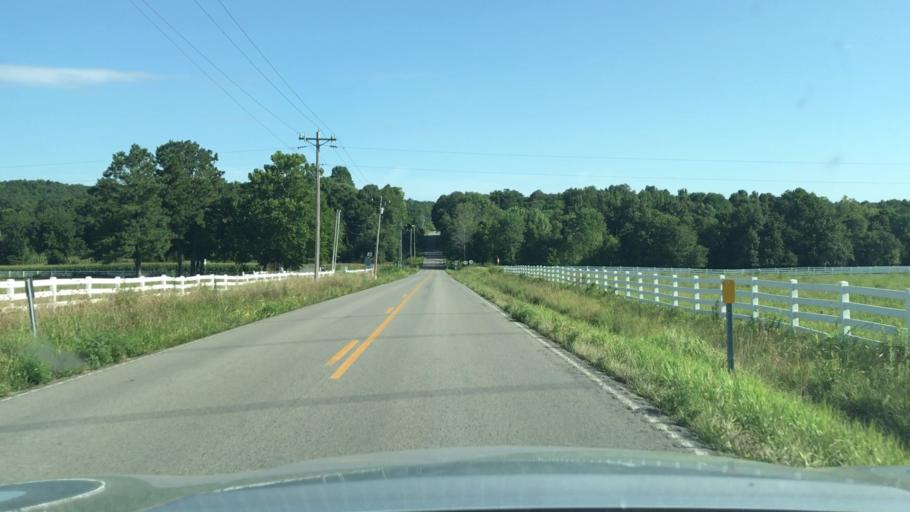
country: US
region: Kentucky
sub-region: Muhlenberg County
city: Greenville
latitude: 37.1004
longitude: -87.1262
